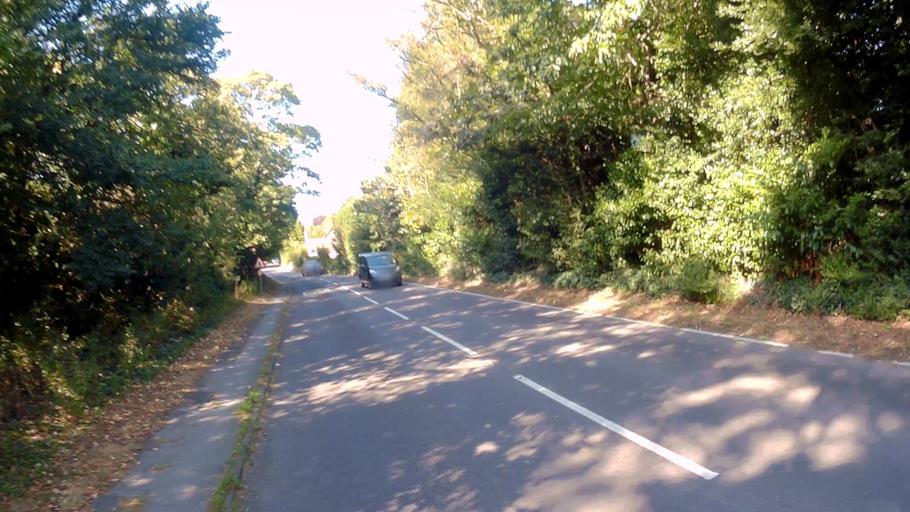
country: GB
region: England
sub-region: Surrey
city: Churt
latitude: 51.1724
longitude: -0.7876
